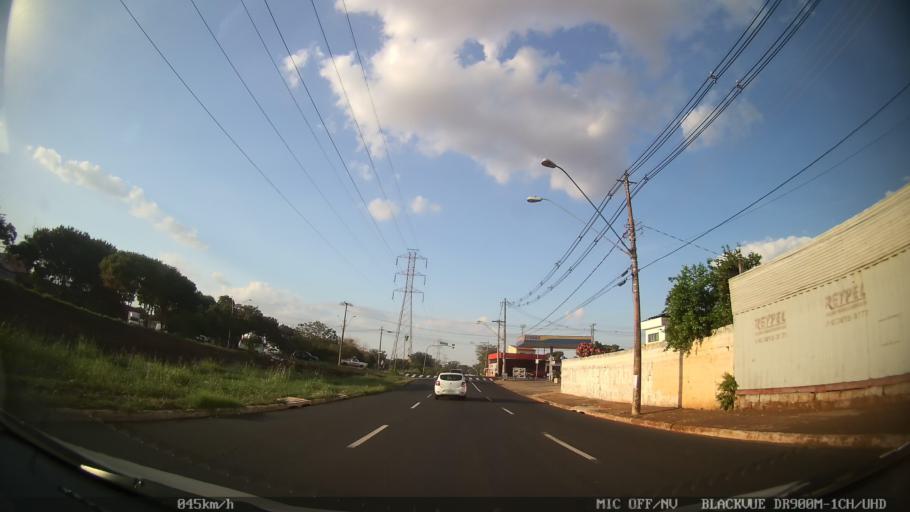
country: BR
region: Sao Paulo
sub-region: Ribeirao Preto
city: Ribeirao Preto
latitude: -21.1479
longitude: -47.8064
